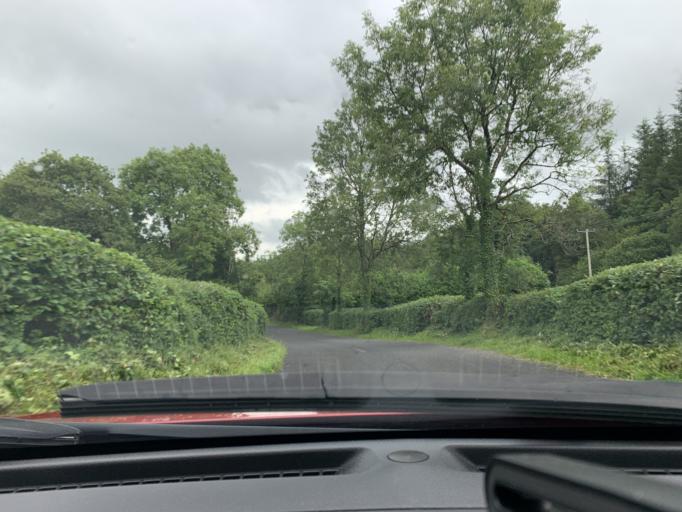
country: IE
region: Connaught
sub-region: County Leitrim
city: Manorhamilton
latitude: 54.3108
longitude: -8.2055
